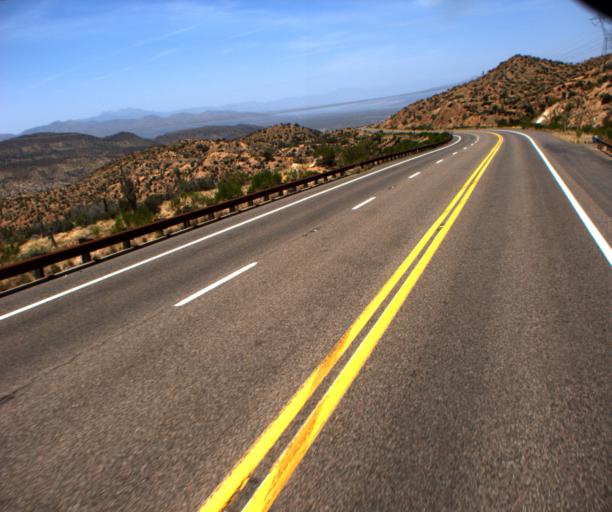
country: US
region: Arizona
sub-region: Gila County
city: Miami
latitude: 33.5431
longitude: -110.9388
